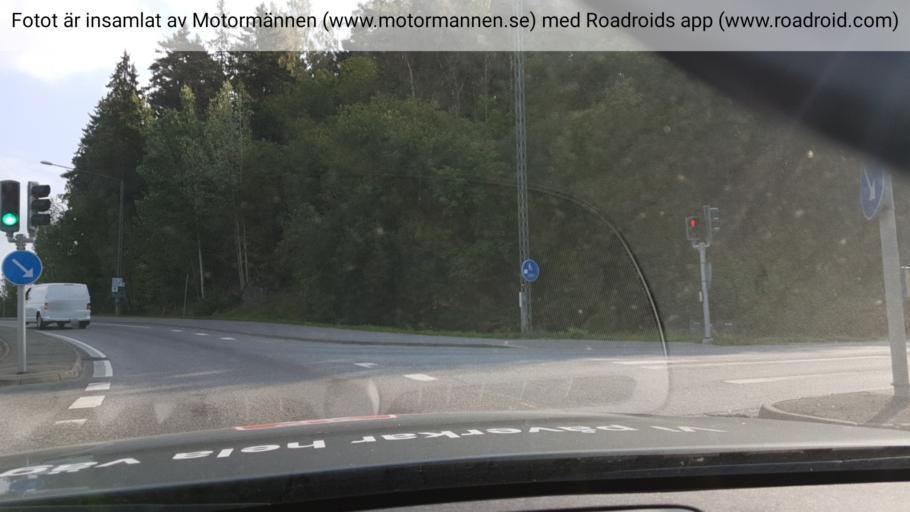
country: SE
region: Stockholm
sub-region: Botkyrka Kommun
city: Tumba
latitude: 59.1980
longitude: 17.8389
